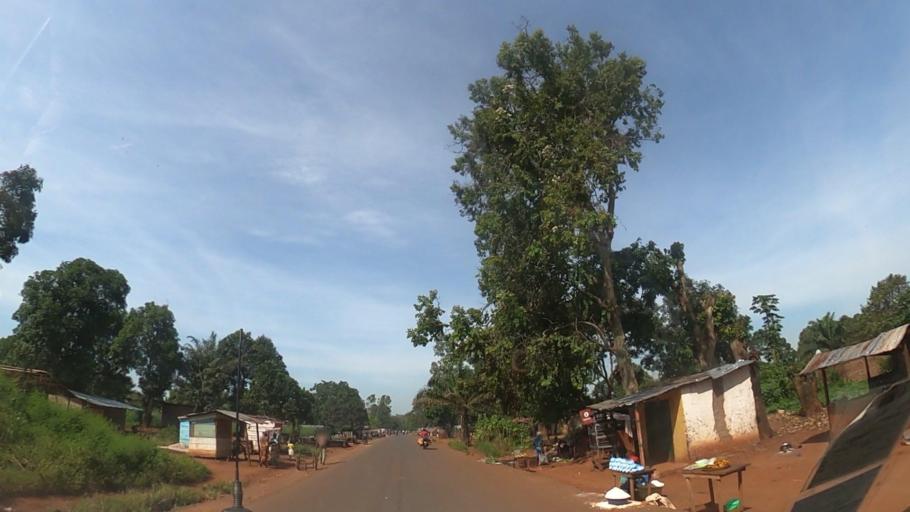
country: CF
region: Bangui
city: Bangui
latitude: 4.3131
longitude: 18.4878
